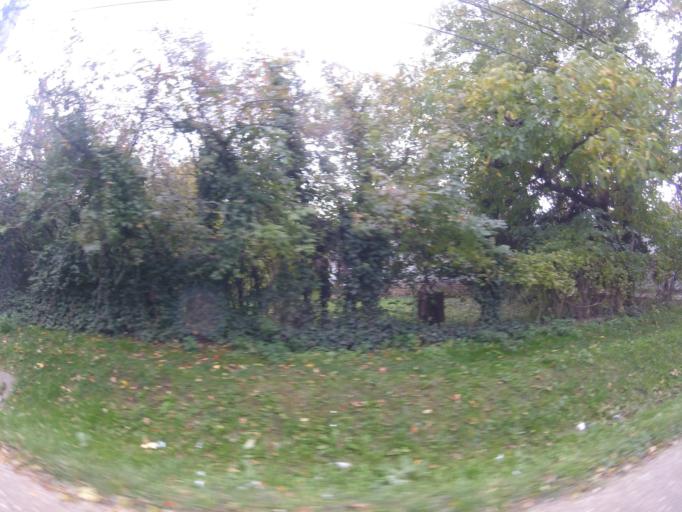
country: HU
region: Pest
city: Csobanka
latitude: 47.6446
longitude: 18.9626
